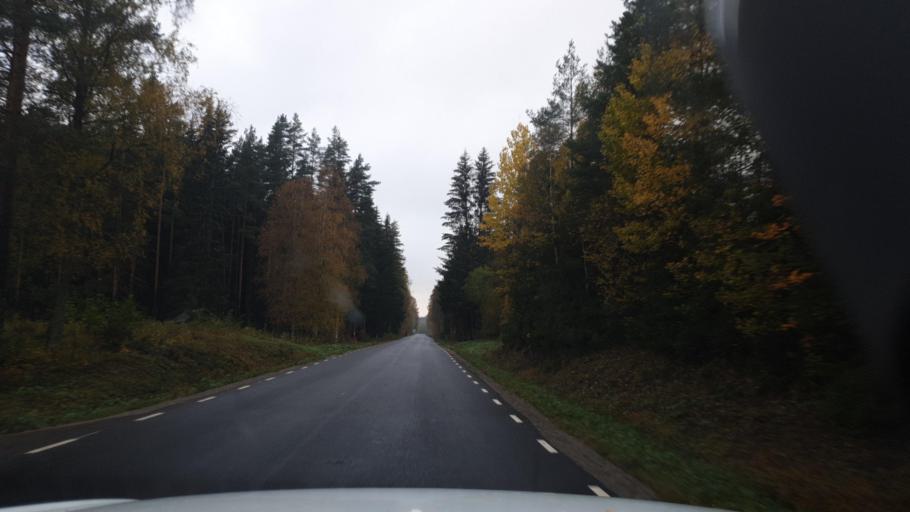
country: SE
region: Vaermland
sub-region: Arvika Kommun
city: Arvika
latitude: 59.6534
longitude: 12.7319
